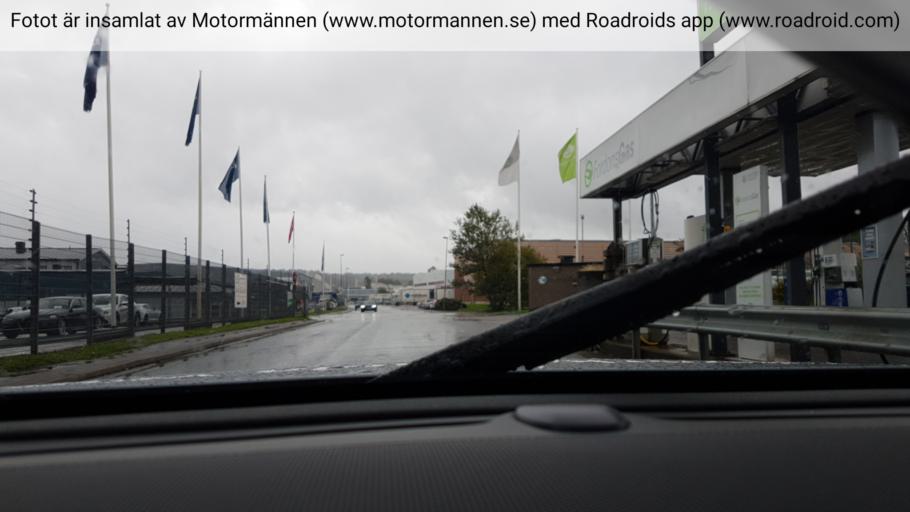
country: SE
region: Vaestra Goetaland
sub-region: Molndal
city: Moelndal
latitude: 57.6415
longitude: 12.0081
